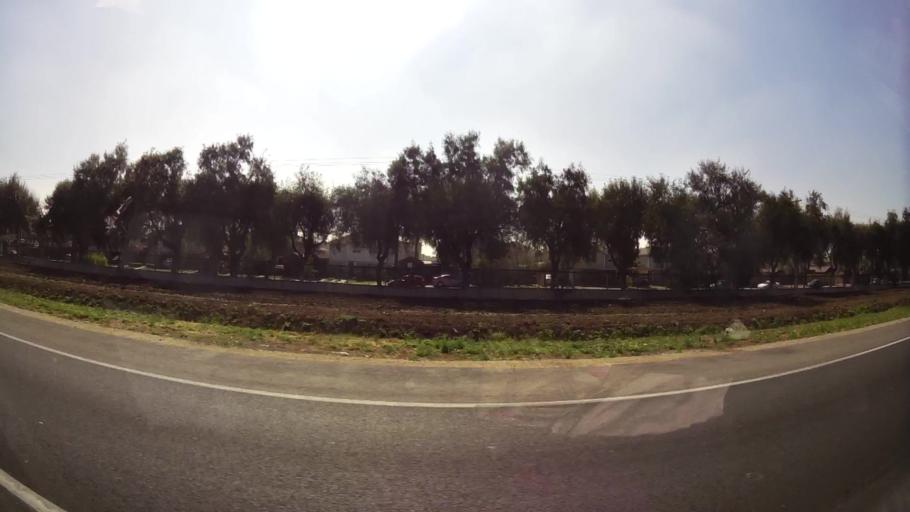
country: CL
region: Santiago Metropolitan
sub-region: Provincia de Santiago
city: Lo Prado
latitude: -33.4944
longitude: -70.7721
